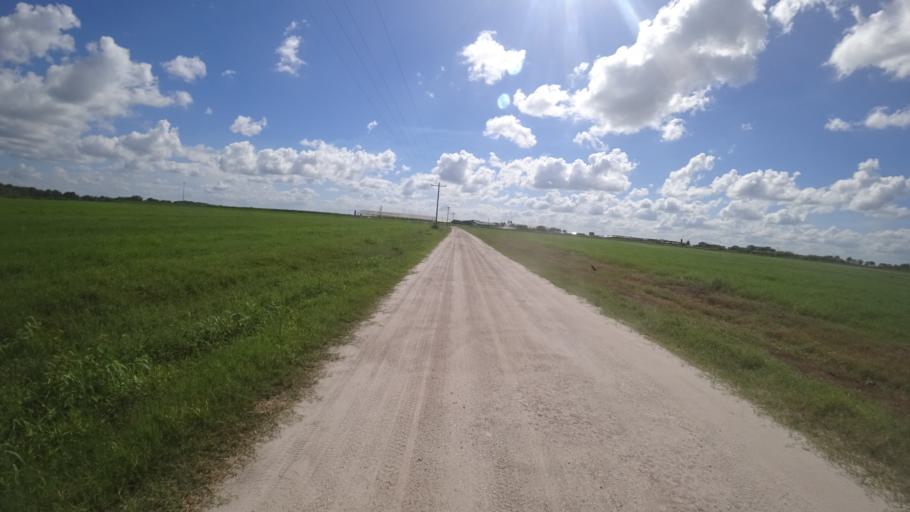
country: US
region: Florida
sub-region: DeSoto County
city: Arcadia
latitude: 27.3169
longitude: -82.1249
